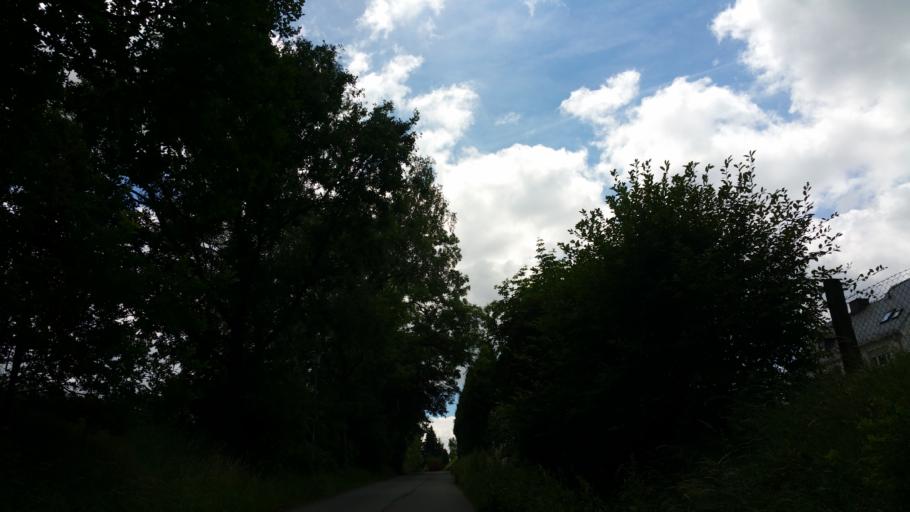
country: DE
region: Bavaria
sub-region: Upper Franconia
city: Schwarzenbach an der Saale
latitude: 50.2160
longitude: 11.9328
